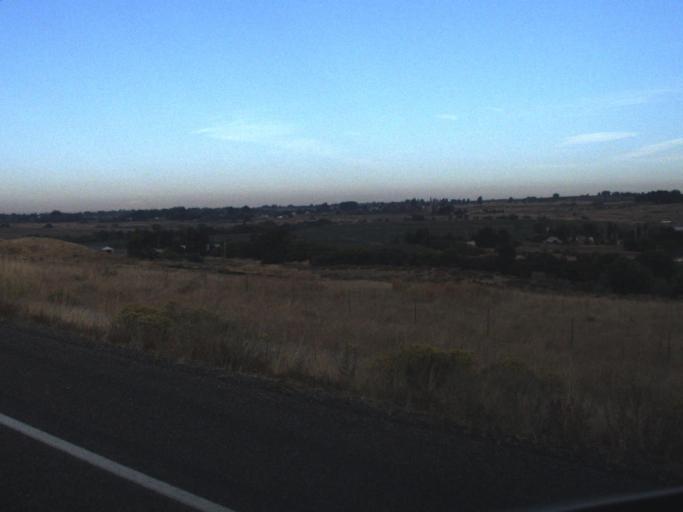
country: US
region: Washington
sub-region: Benton County
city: Prosser
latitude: 46.2412
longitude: -119.6403
